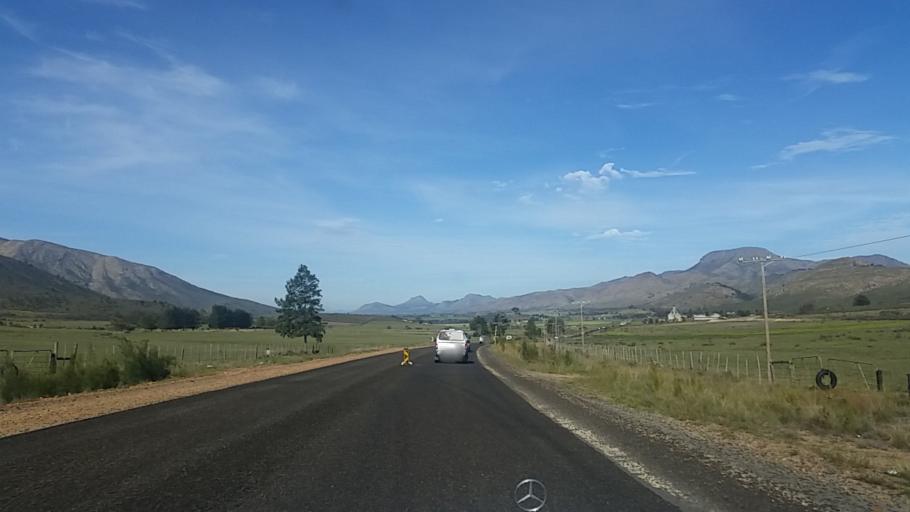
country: ZA
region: Western Cape
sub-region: Eden District Municipality
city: George
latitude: -33.8267
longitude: 22.4099
